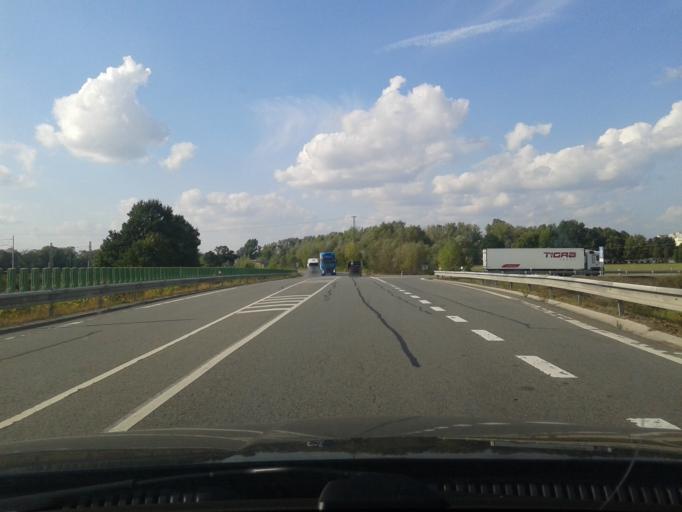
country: CZ
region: Moravskoslezsky
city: Stary Bohumin
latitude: 49.9117
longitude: 18.3302
